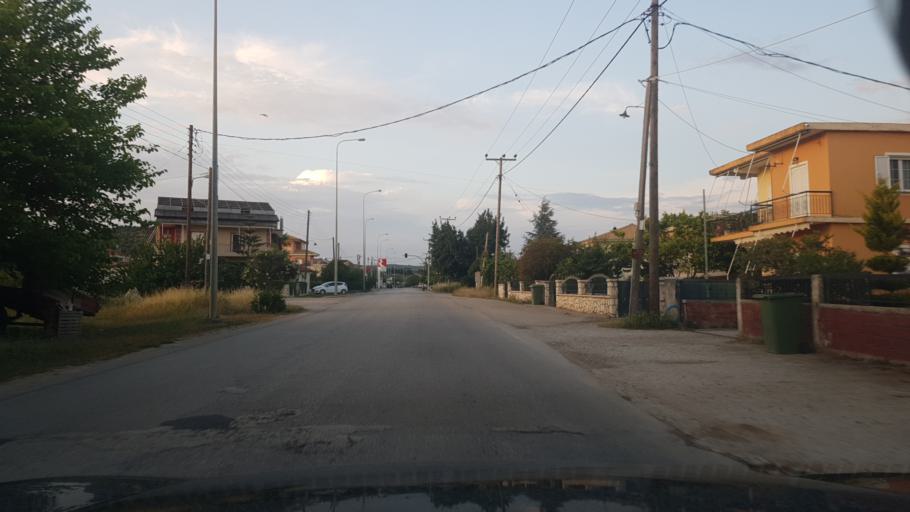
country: GR
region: West Greece
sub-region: Nomos Aitolias kai Akarnanias
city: Vonitsa
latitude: 38.8667
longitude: 20.8026
